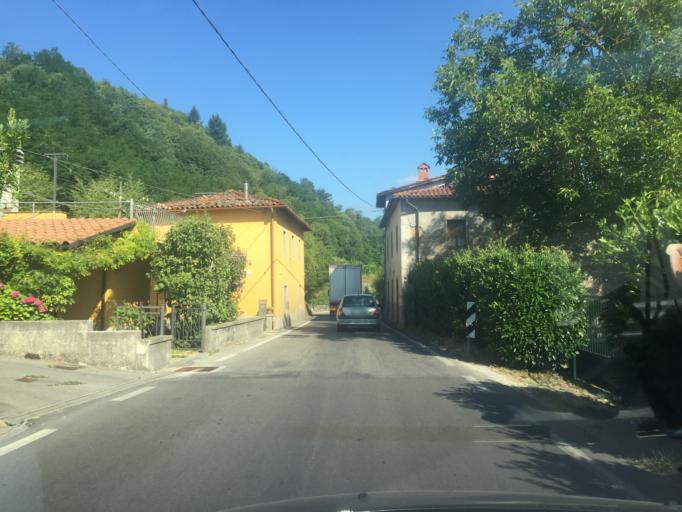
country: IT
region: Tuscany
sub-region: Provincia di Lucca
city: San Romano in Garfagnana
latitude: 44.1387
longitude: 10.3666
